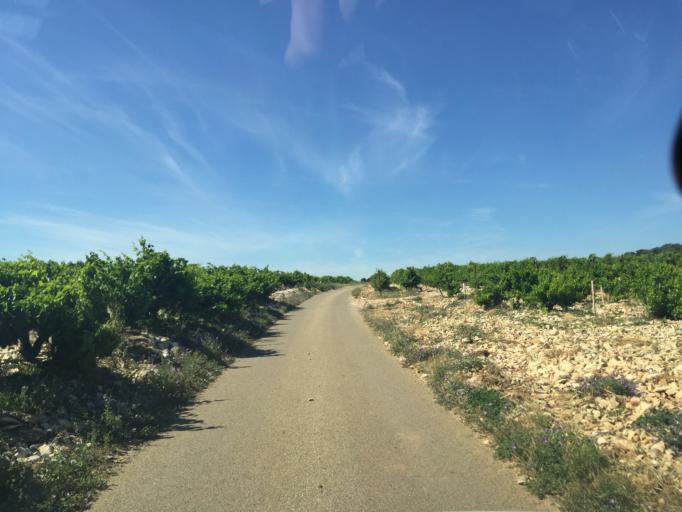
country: FR
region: Provence-Alpes-Cote d'Azur
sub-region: Departement du Vaucluse
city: Chateauneuf-du-Pape
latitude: 44.0694
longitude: 4.8064
